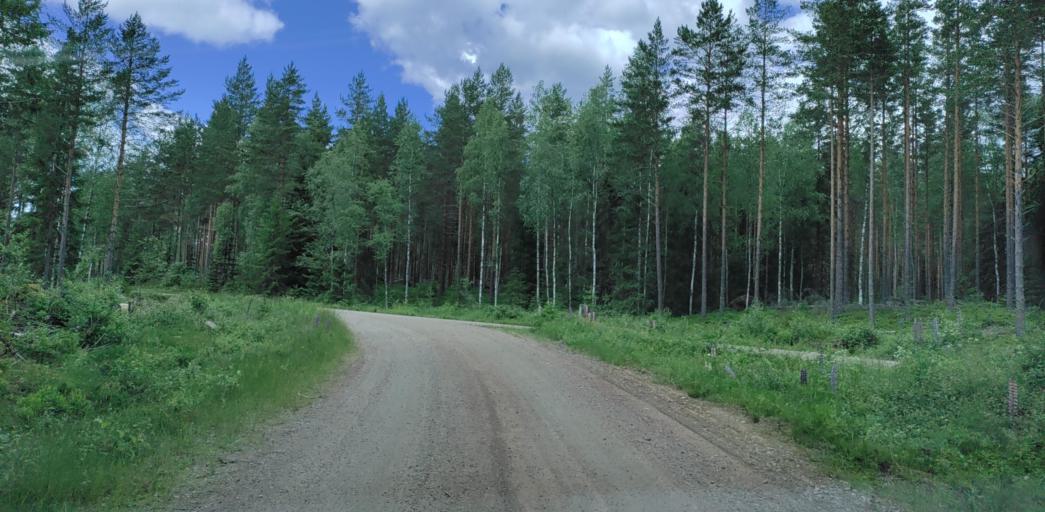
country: SE
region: Vaermland
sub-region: Hagfors Kommun
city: Ekshaerad
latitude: 60.0929
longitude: 13.4077
